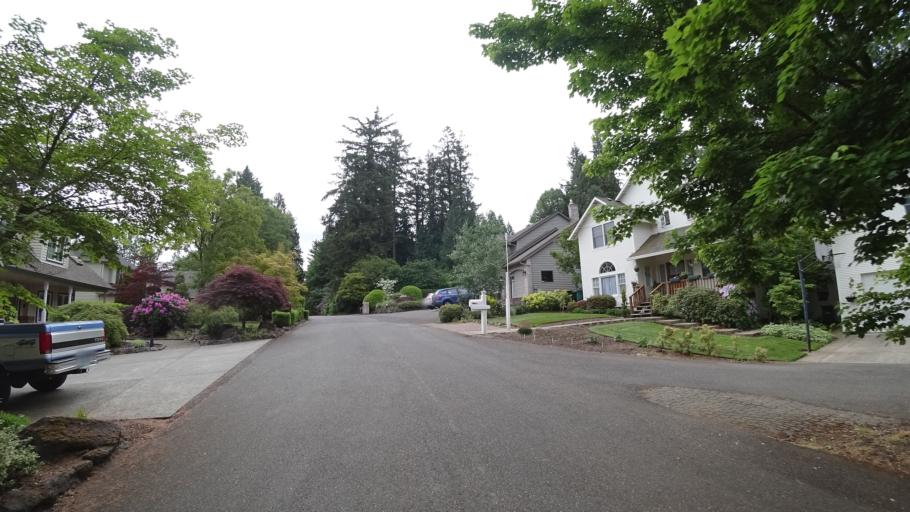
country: US
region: Oregon
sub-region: Washington County
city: Garden Home-Whitford
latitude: 45.4705
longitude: -122.7533
